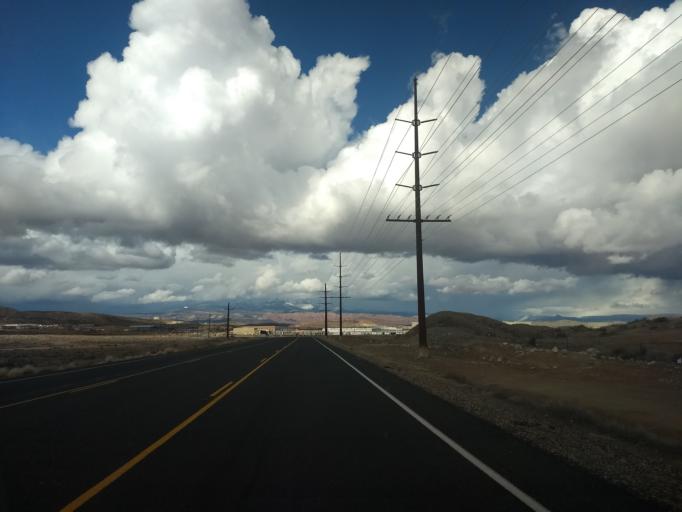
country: US
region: Utah
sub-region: Washington County
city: Saint George
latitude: 37.0199
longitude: -113.5637
